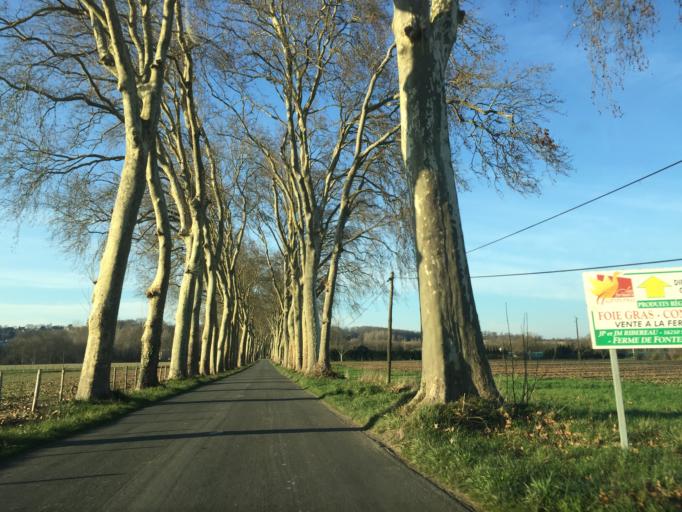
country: FR
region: Aquitaine
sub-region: Departement de la Dordogne
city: Saint-Aulaye
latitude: 45.2657
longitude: 0.1845
